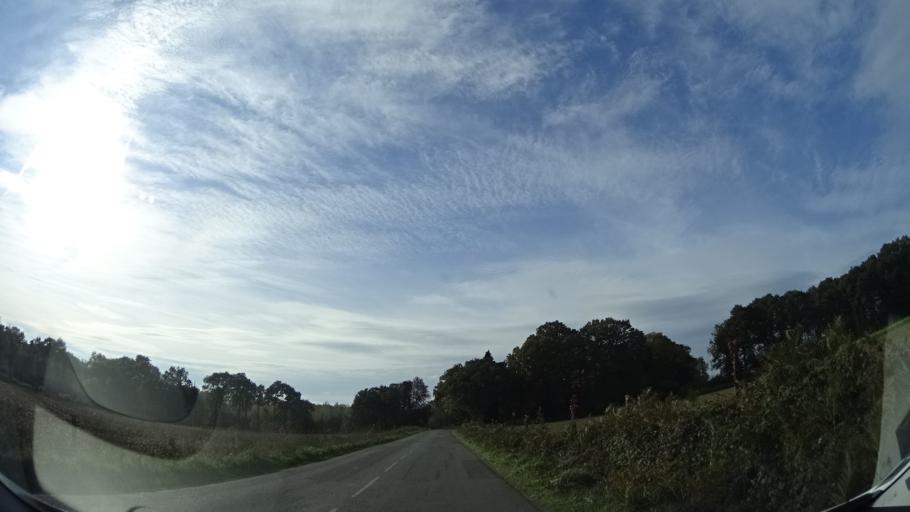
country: FR
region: Brittany
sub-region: Departement d'Ille-et-Vilaine
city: Romille
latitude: 48.2140
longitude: -1.9158
